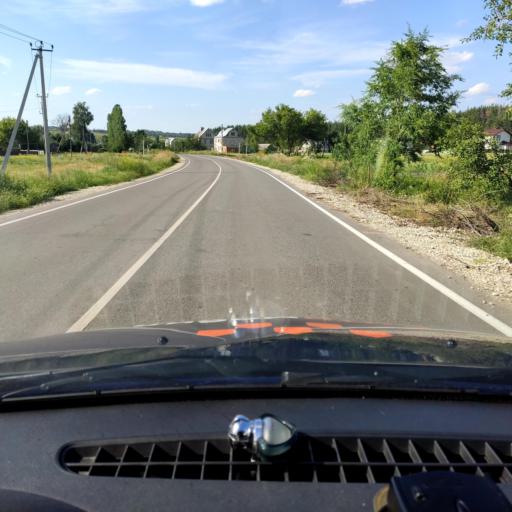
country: RU
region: Voronezj
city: Devitsa
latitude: 51.6507
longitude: 38.9727
